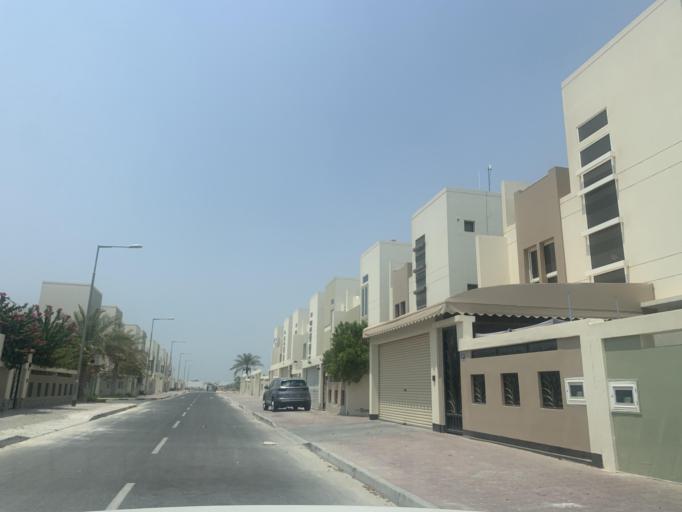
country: BH
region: Central Governorate
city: Madinat Hamad
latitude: 26.1355
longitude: 50.4671
